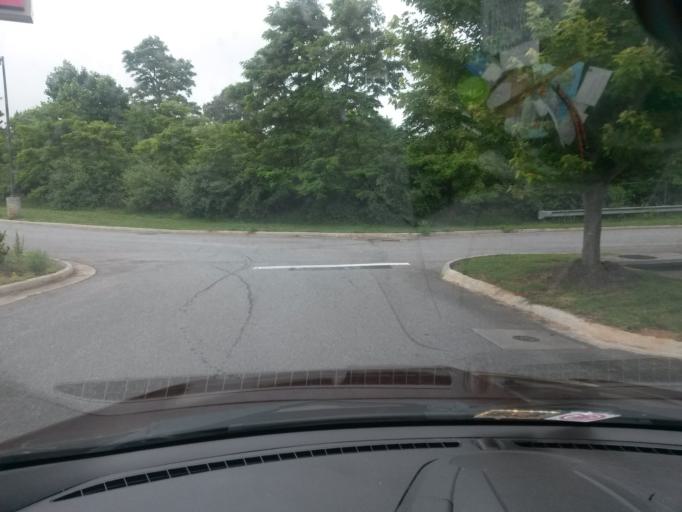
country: US
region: Virginia
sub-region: City of Bedford
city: Bedford
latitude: 37.3205
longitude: -79.4852
